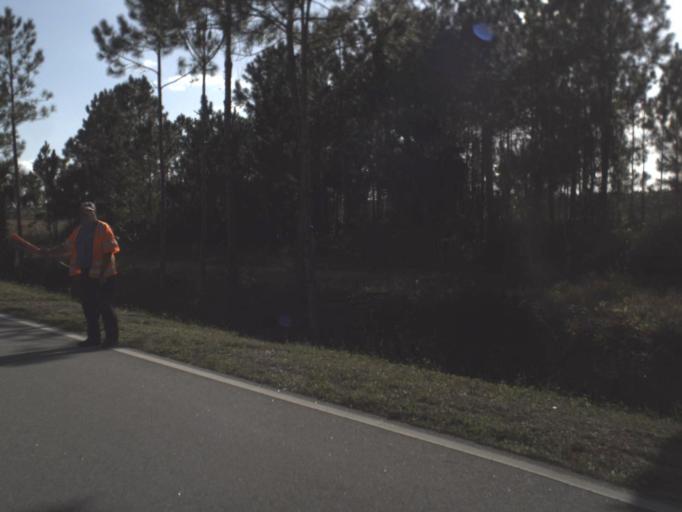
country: US
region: Florida
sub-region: Volusia County
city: Holly Hill
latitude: 29.2292
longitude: -81.0956
